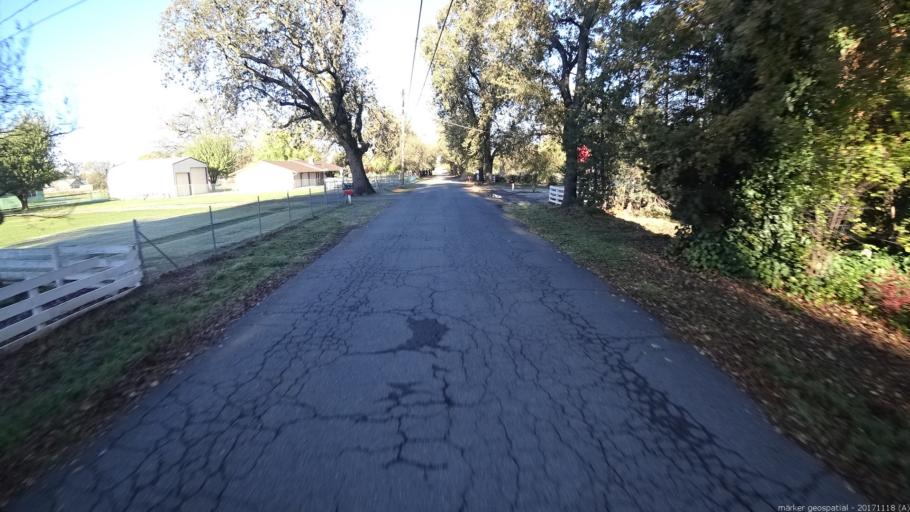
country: US
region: California
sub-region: Shasta County
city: Anderson
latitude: 40.4497
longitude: -122.2799
